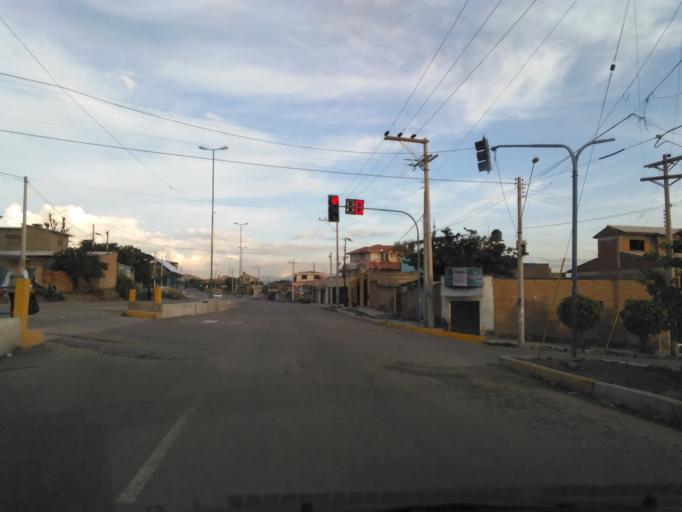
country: BO
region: Cochabamba
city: Cochabamba
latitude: -17.3498
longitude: -66.1710
